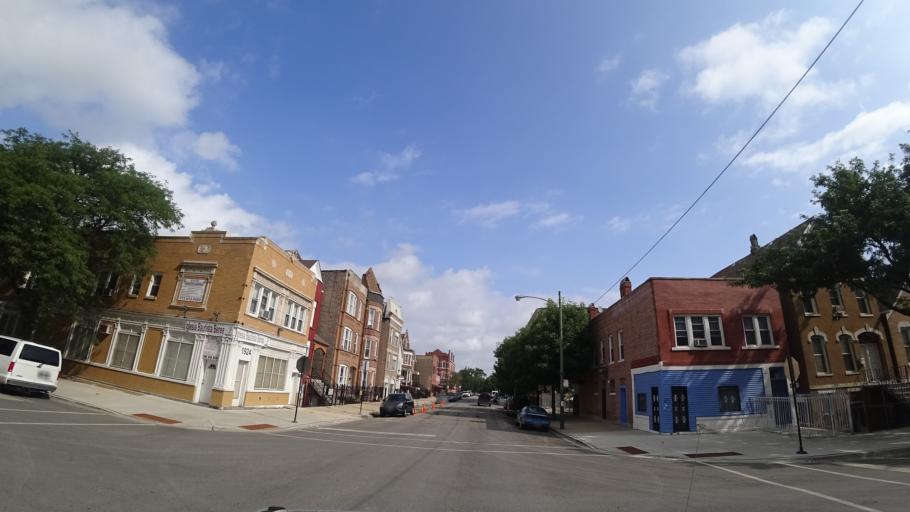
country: US
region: Illinois
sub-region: Cook County
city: Chicago
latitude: 41.8548
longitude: -87.6808
